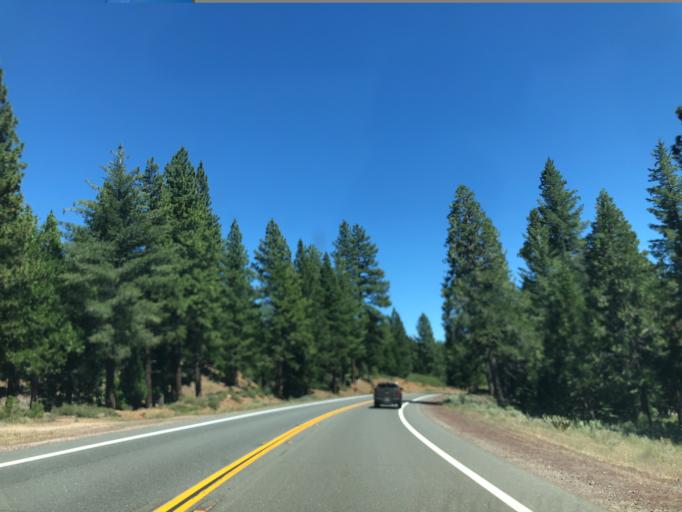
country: US
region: California
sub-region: Lassen County
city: Susanville
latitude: 40.4393
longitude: -120.8357
